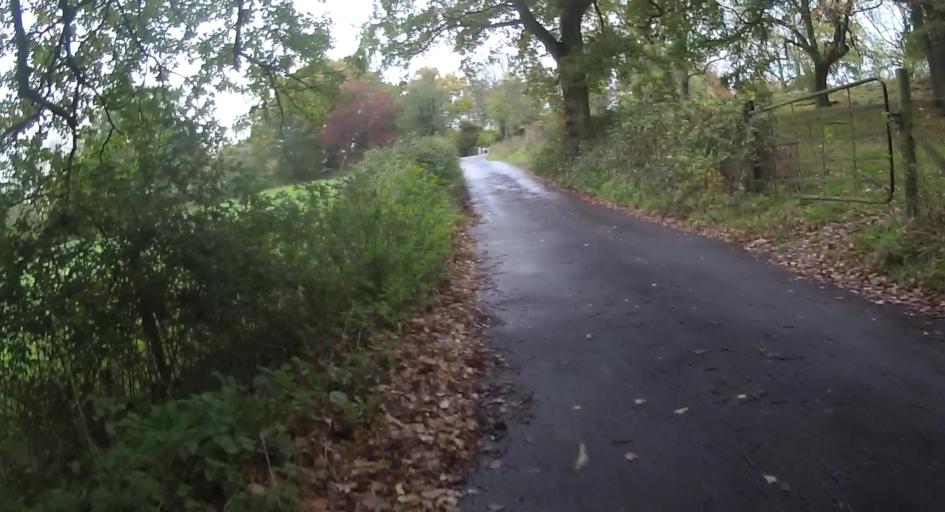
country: GB
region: England
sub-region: Surrey
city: Farnham
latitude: 51.2208
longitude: -0.8318
